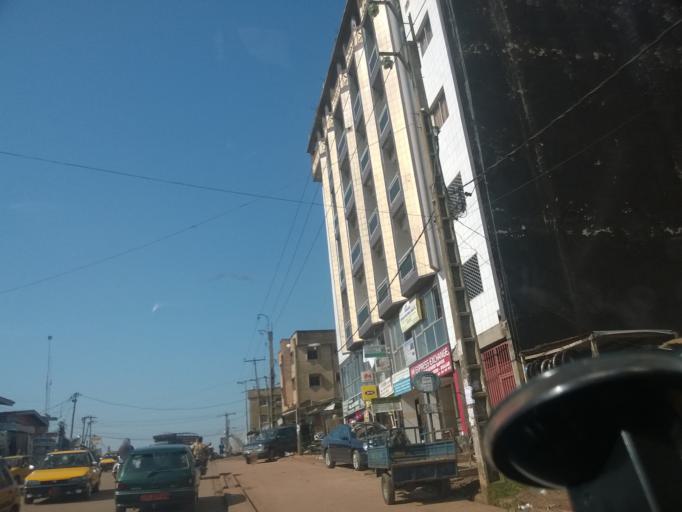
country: CM
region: Centre
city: Yaounde
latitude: 3.8290
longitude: 11.4801
